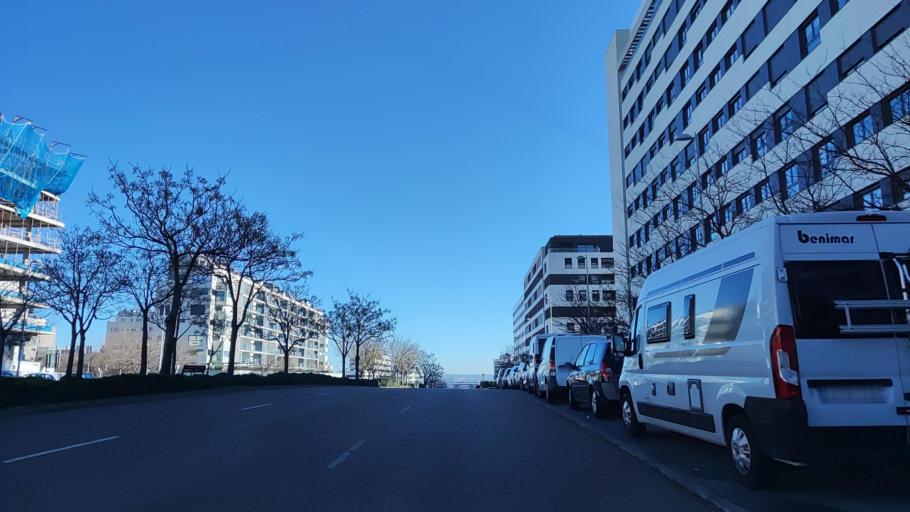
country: ES
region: Madrid
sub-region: Provincia de Madrid
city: Hortaleza
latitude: 40.4939
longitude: -3.6193
